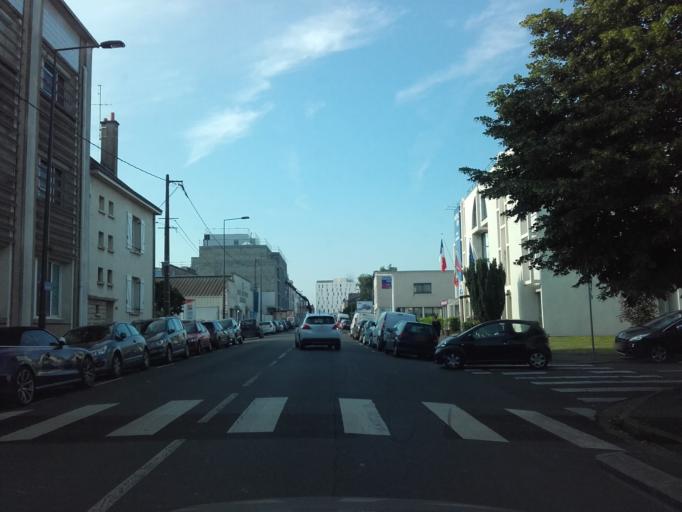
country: FR
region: Centre
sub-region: Departement d'Indre-et-Loire
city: Tours
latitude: 47.3789
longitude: 0.6775
